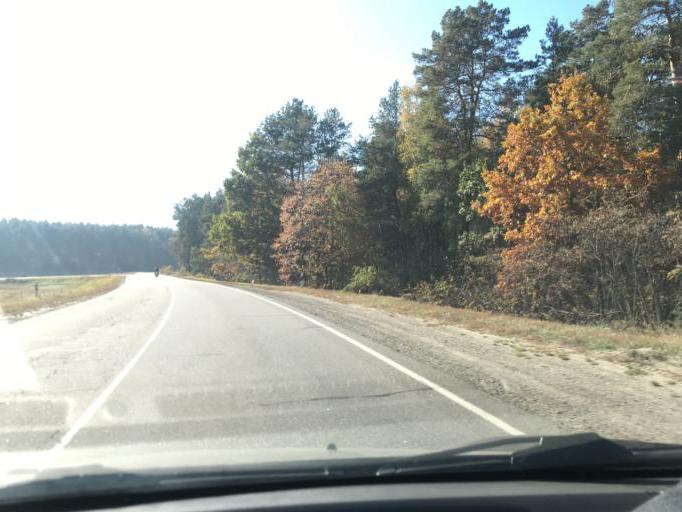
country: BY
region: Gomel
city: Gomel
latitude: 52.3892
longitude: 30.8257
